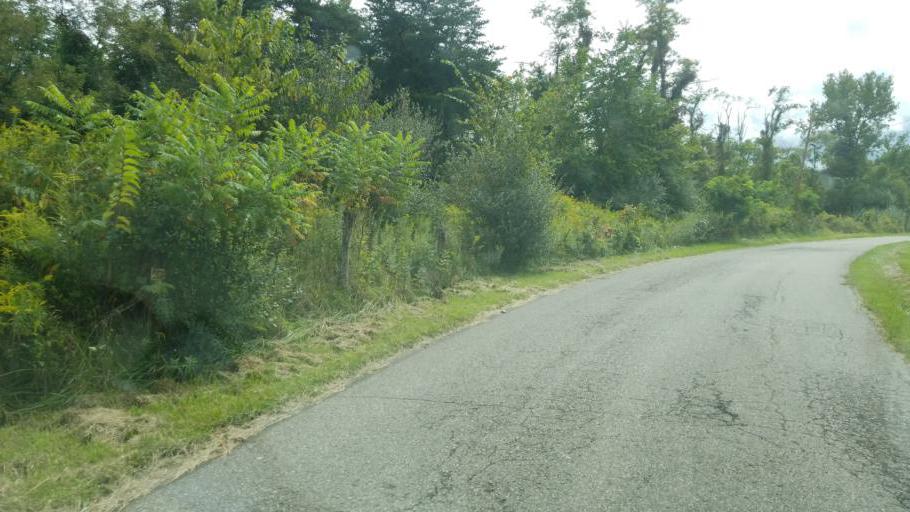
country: US
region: Ohio
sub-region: Jackson County
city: Oak Hill
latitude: 38.8967
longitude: -82.6229
